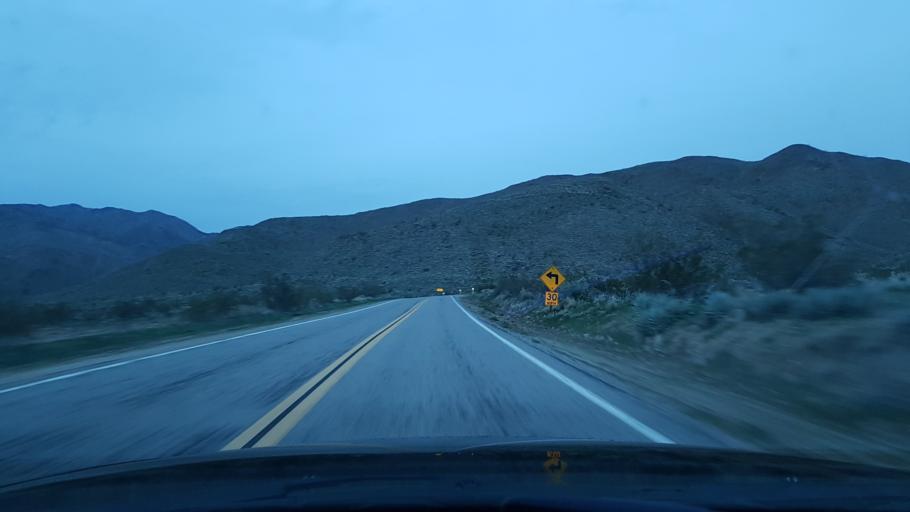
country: US
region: California
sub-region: San Diego County
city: Julian
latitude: 32.9958
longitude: -116.4475
